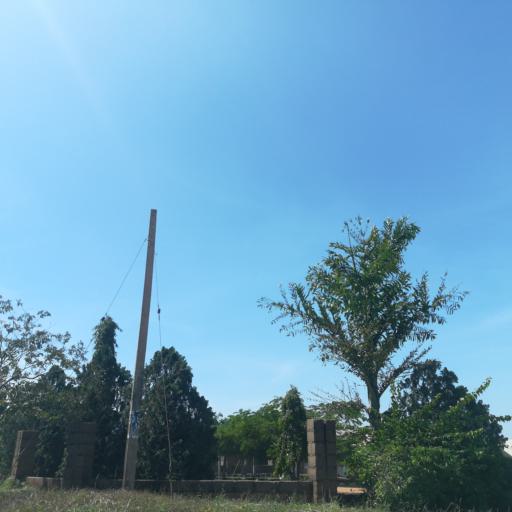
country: NG
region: Plateau
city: Bukuru
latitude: 9.7806
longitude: 8.8858
